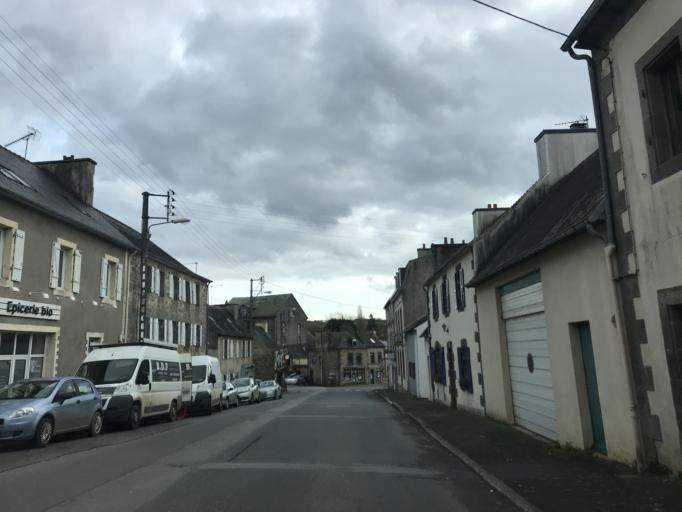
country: FR
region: Brittany
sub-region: Departement du Finistere
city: Le Faou
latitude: 48.2978
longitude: -4.1817
